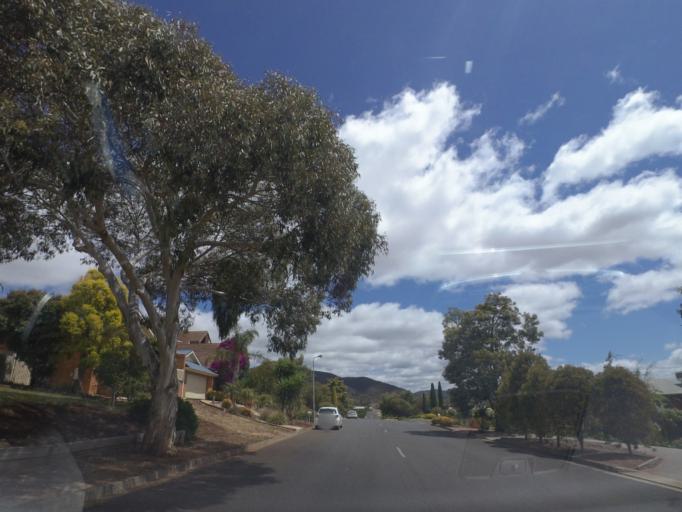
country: AU
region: Victoria
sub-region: Moorabool
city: Bacchus Marsh
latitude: -37.6385
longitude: 144.4256
